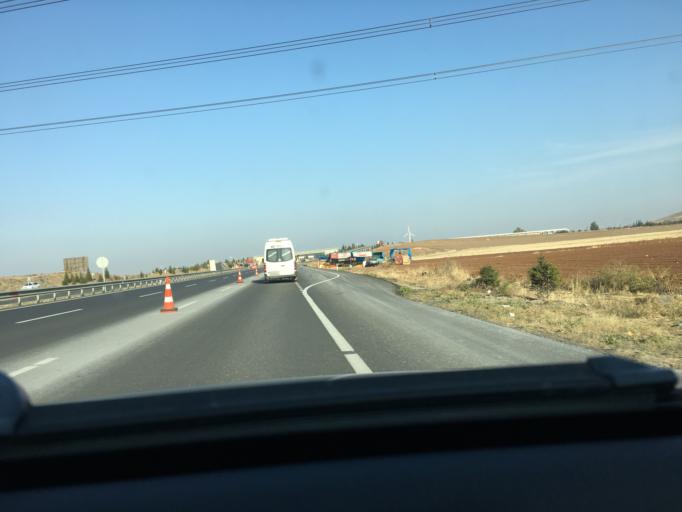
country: TR
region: Ankara
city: Temelli
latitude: 39.7113
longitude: 32.2905
